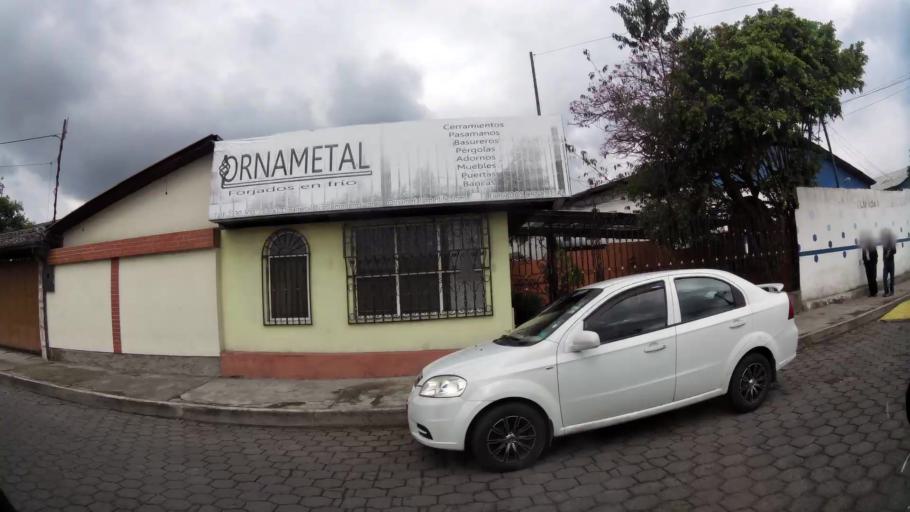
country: EC
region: Pichincha
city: Sangolqui
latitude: -0.3401
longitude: -78.4536
